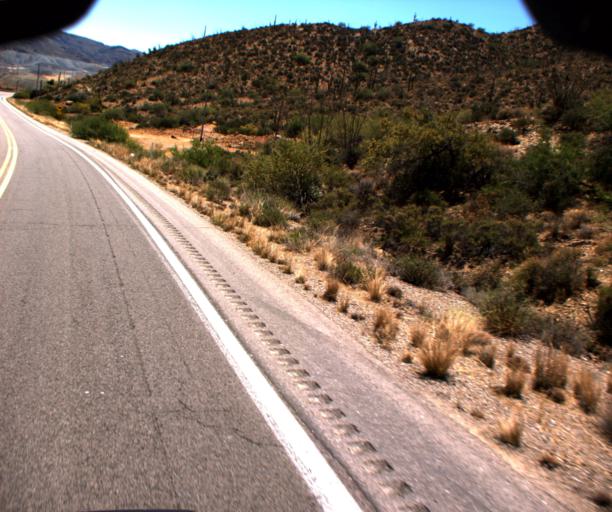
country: US
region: Arizona
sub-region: Pinal County
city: Superior
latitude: 33.1724
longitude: -111.0152
